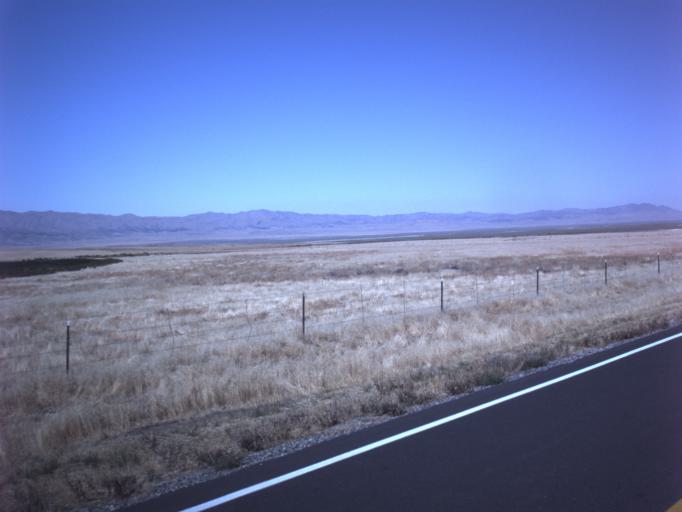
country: US
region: Utah
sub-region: Tooele County
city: Grantsville
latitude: 40.4390
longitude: -112.7486
